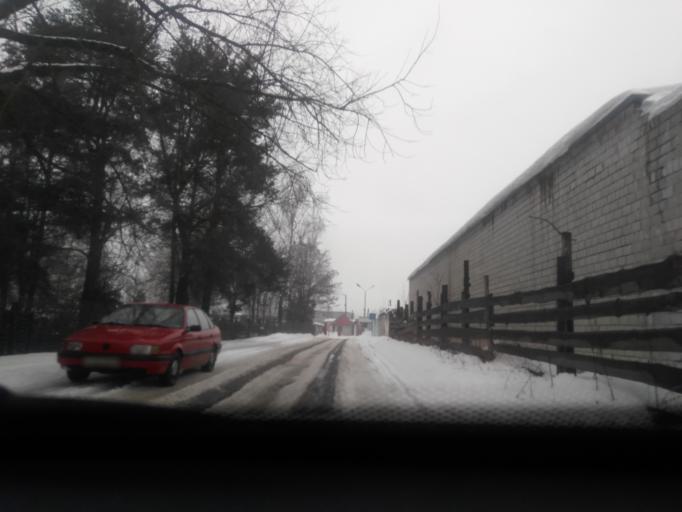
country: BY
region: Mogilev
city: Babruysk
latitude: 53.1689
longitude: 29.2102
